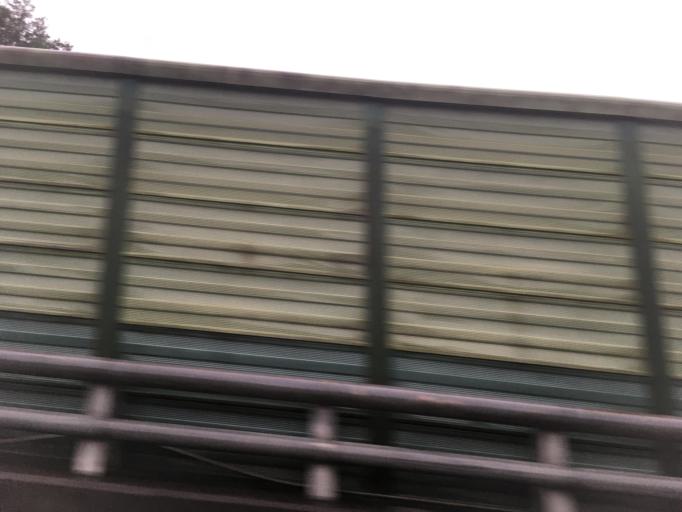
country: TW
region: Taiwan
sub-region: Keelung
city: Keelung
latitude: 25.0340
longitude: 121.8633
